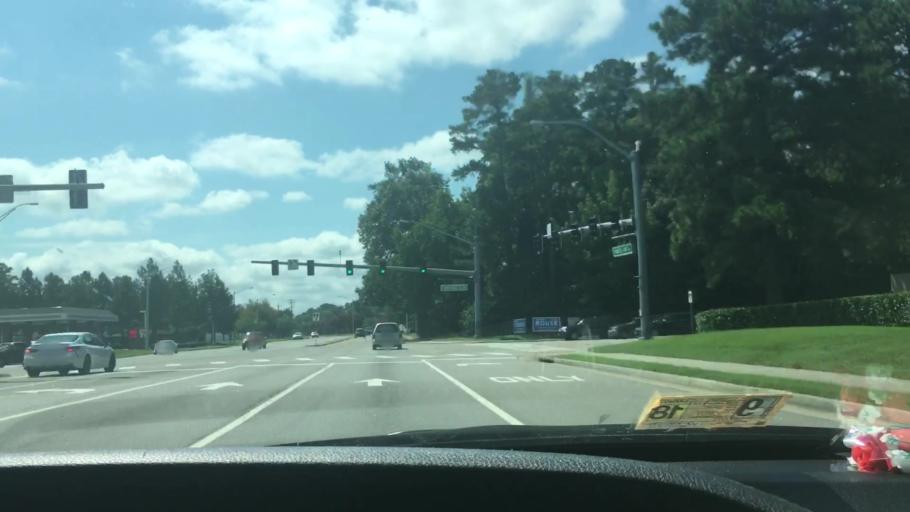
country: US
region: Virginia
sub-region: City of Chesapeake
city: Chesapeake
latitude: 36.8045
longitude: -76.1333
